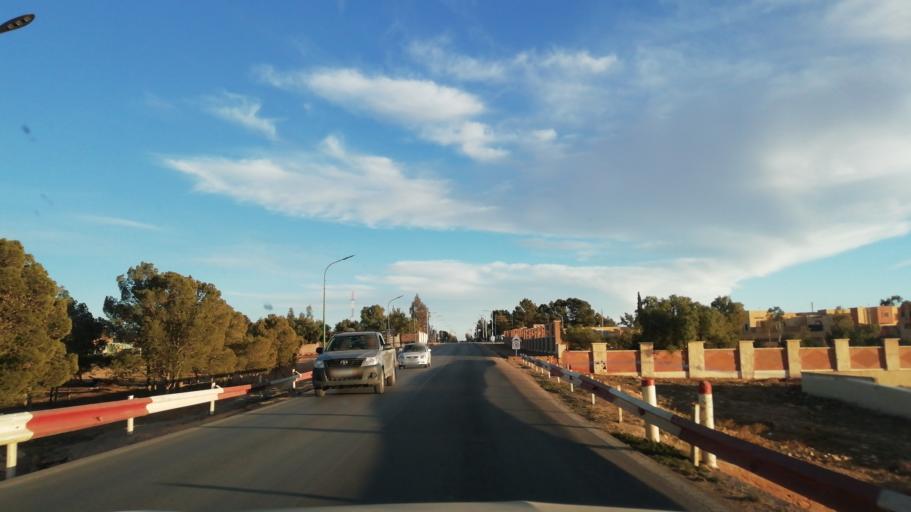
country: DZ
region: Wilaya de Naama
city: Naama
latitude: 33.7205
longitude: -0.7338
